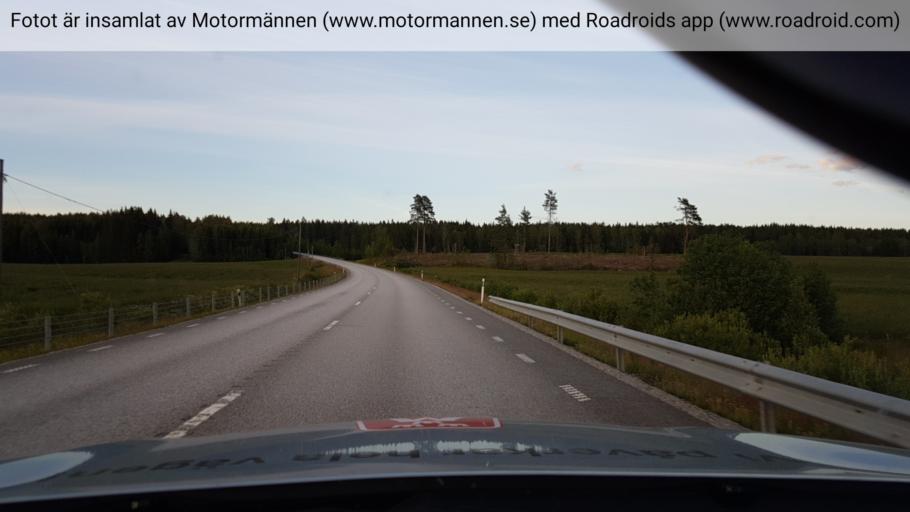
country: SE
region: Vaestmanland
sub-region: Skinnskattebergs Kommun
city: Skinnskatteberg
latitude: 59.7516
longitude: 15.4440
